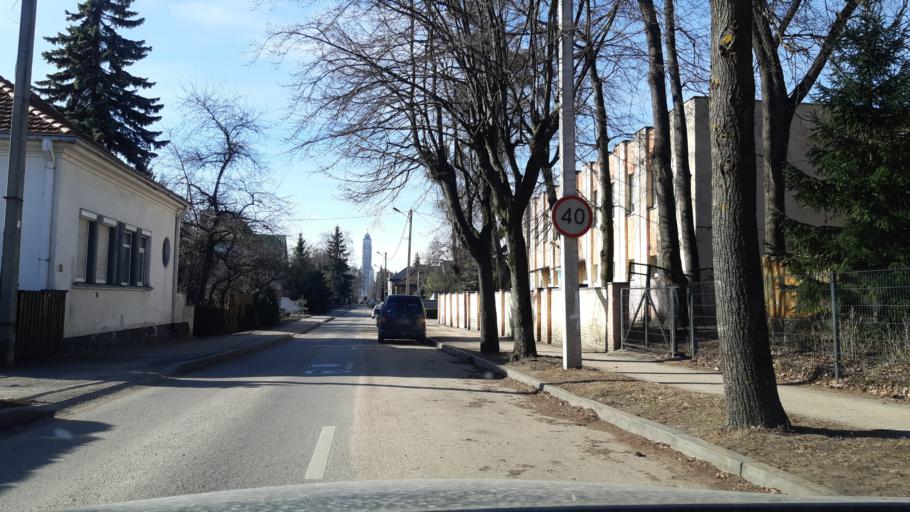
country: LT
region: Kauno apskritis
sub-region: Kaunas
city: Eiguliai
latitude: 54.9059
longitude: 23.9261
